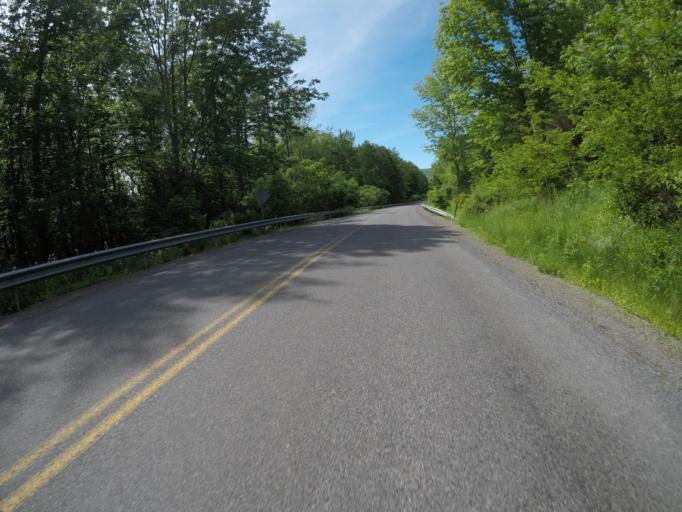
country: US
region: New York
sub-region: Sullivan County
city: Livingston Manor
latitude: 42.0900
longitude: -74.8192
